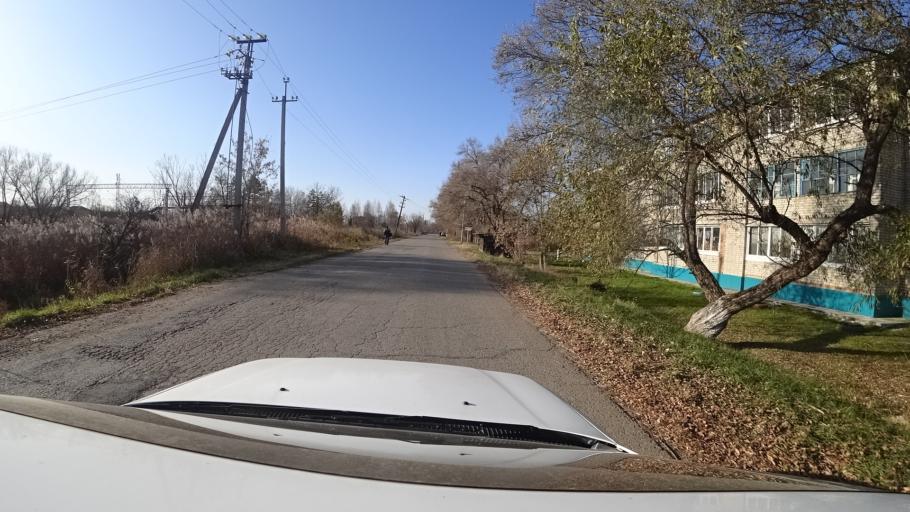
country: RU
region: Primorskiy
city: Lazo
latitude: 45.8784
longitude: 133.6456
